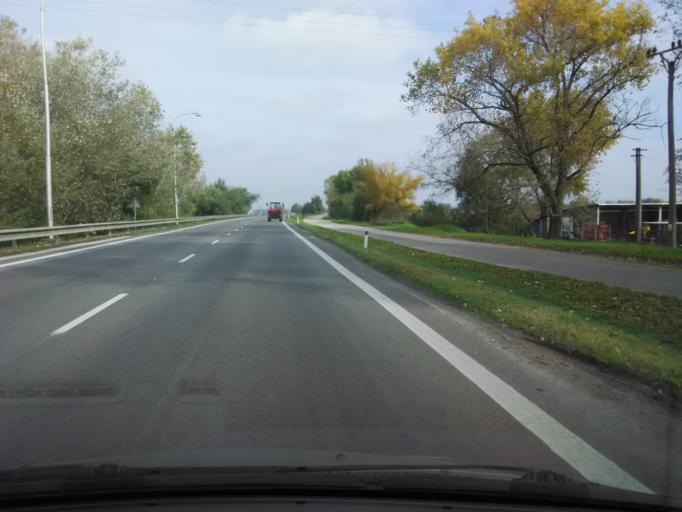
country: SK
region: Nitriansky
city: Komarno
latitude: 47.7883
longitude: 18.1691
